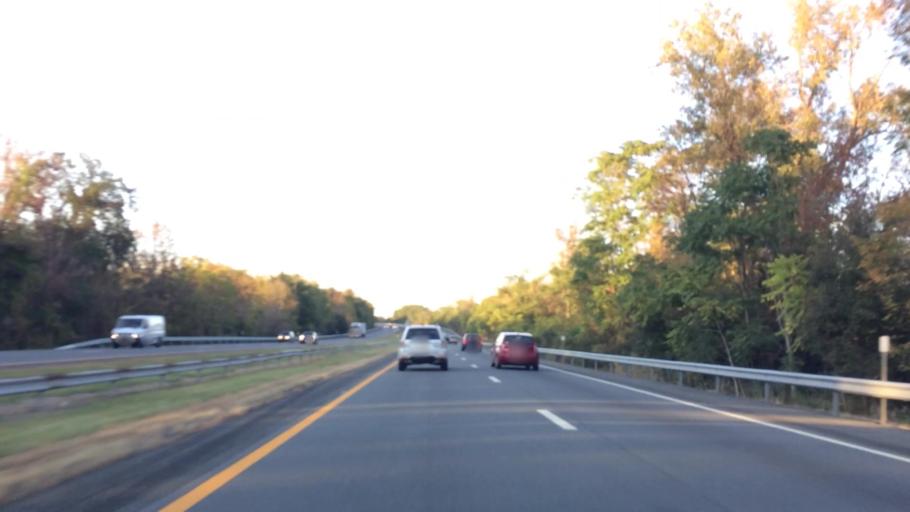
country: US
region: New York
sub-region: Orange County
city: Vails Gate
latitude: 41.4469
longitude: -74.0655
